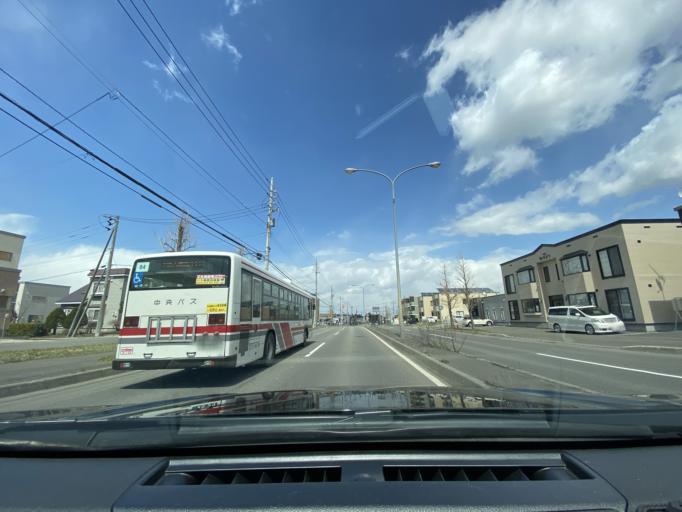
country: JP
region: Hokkaido
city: Kitahiroshima
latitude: 42.9814
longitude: 141.4838
